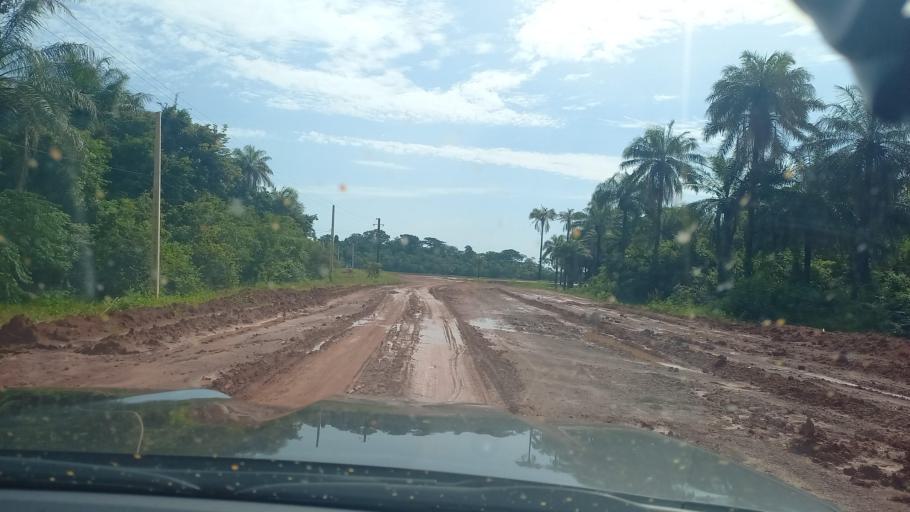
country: SN
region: Ziguinchor
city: Ziguinchor
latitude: 12.6734
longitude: -16.2050
